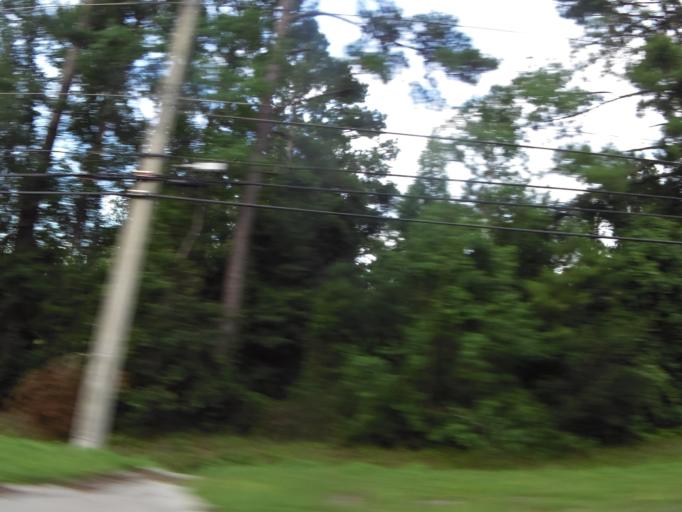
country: US
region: Florida
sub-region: Duval County
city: Jacksonville
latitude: 30.3484
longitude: -81.8069
